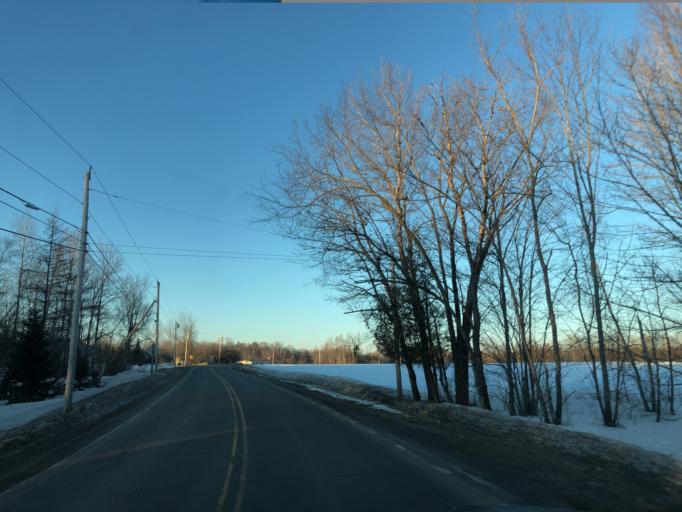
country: US
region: Maine
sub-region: Penobscot County
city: Charleston
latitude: 45.0084
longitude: -69.0127
